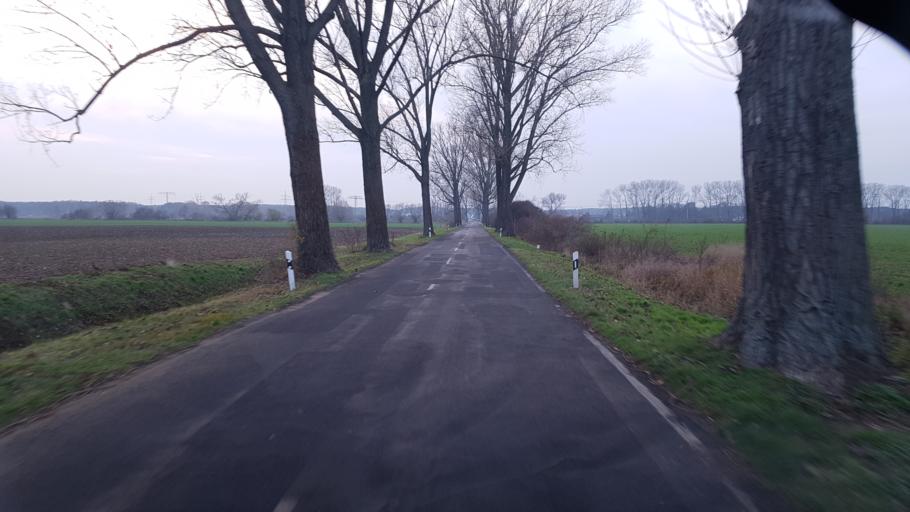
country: DE
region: Brandenburg
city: Ziltendorf
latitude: 52.2130
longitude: 14.6425
